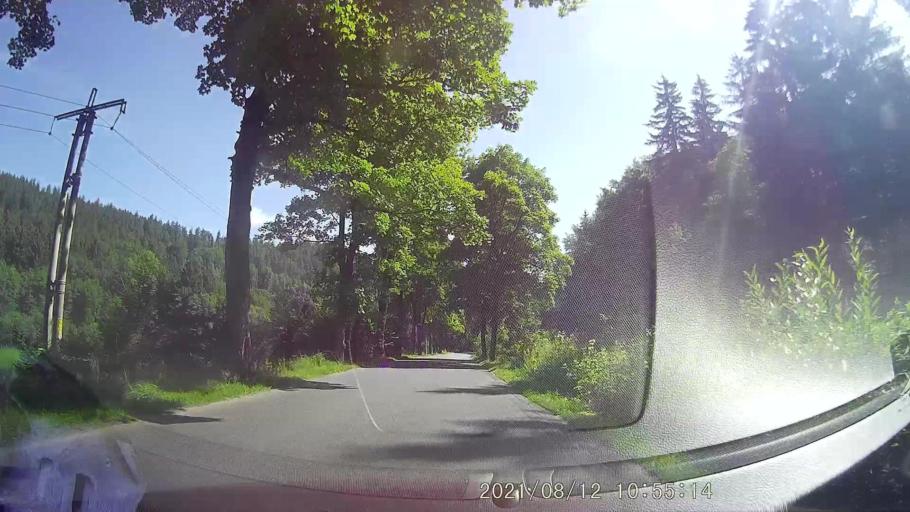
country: PL
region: Lower Silesian Voivodeship
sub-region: Powiat klodzki
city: Szczytna
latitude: 50.4045
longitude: 16.4729
